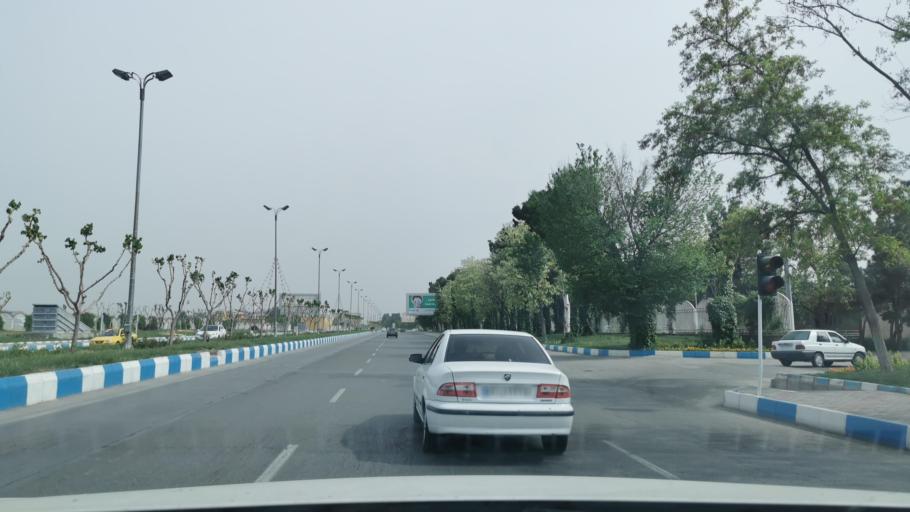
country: IR
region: Razavi Khorasan
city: Mashhad
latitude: 36.2381
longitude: 59.6285
